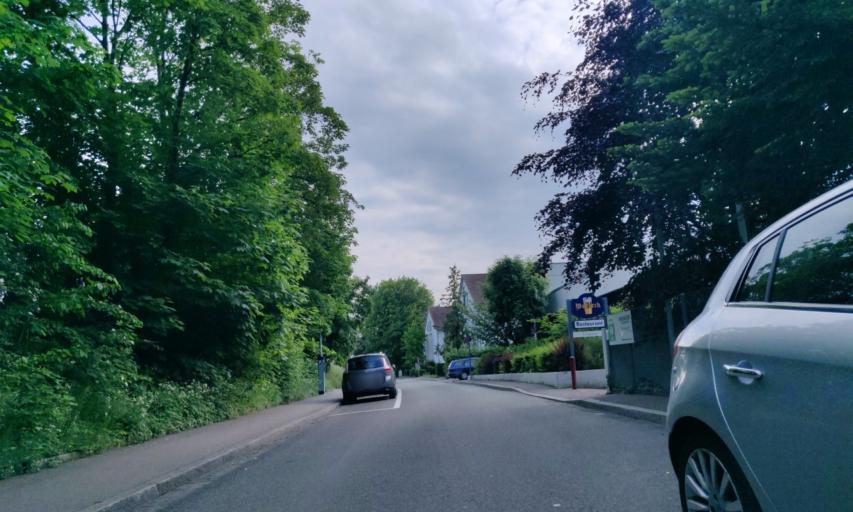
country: CH
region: Basel-Landschaft
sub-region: Bezirk Arlesheim
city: Birsfelden
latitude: 47.5644
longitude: 7.6285
